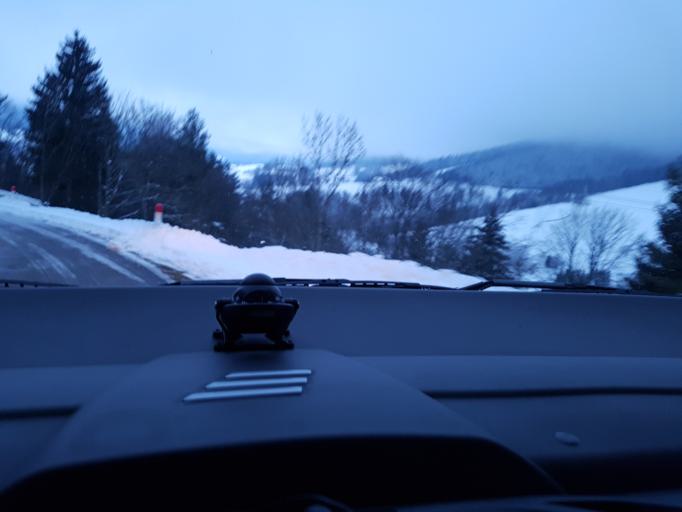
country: FR
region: Alsace
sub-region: Departement du Haut-Rhin
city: Lapoutroie
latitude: 48.1853
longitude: 7.1117
